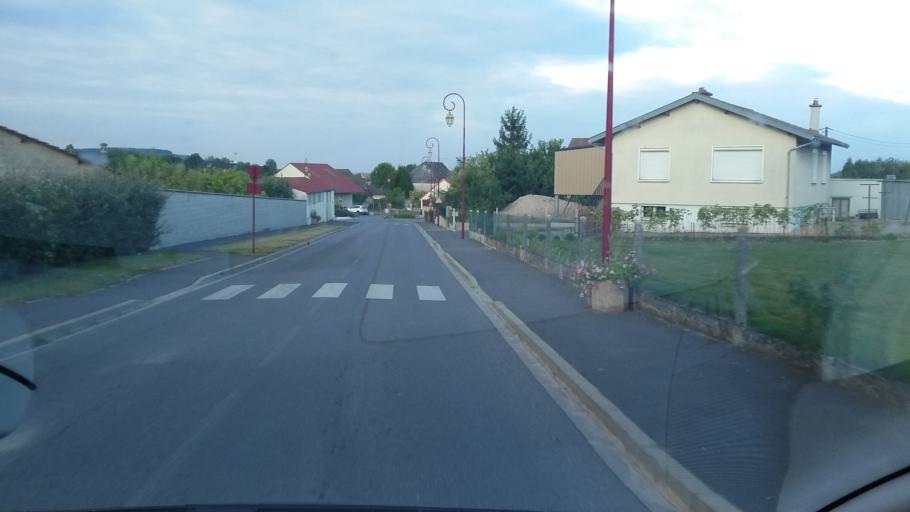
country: FR
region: Champagne-Ardenne
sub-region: Departement de la Marne
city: Vertus
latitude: 48.8762
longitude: 3.9999
